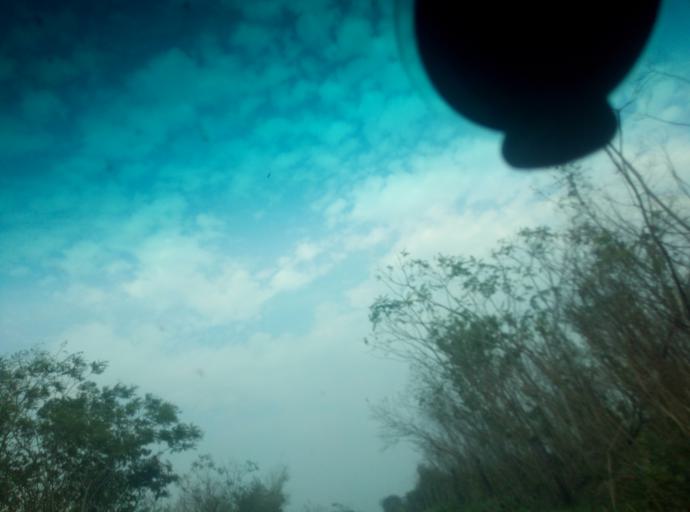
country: PY
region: Caaguazu
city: San Joaquin
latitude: -25.0994
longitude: -56.1350
